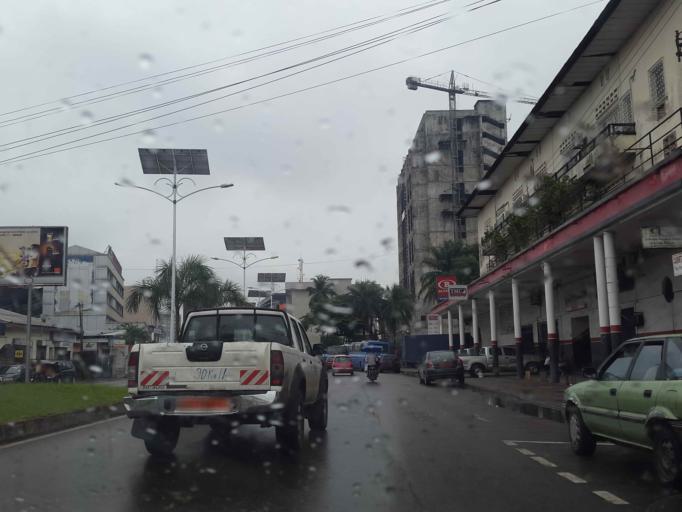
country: CM
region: Littoral
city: Douala
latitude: 4.0576
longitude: 9.7003
